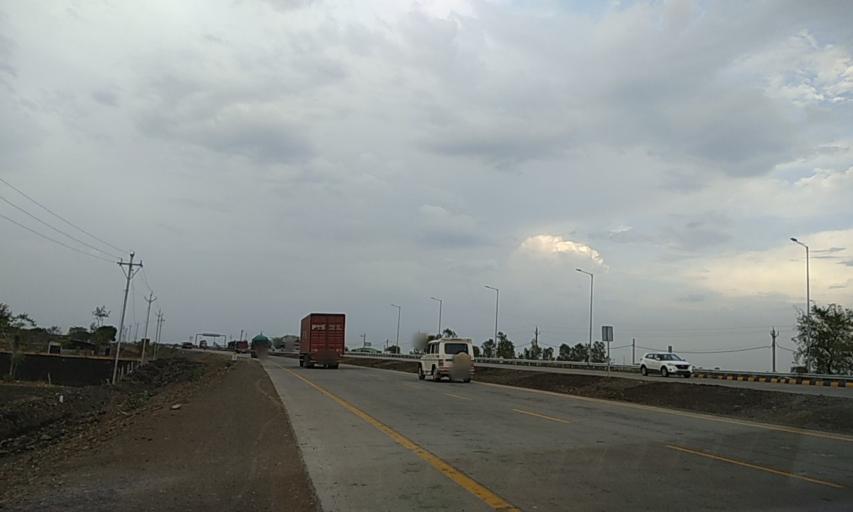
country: IN
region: Madhya Pradesh
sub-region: Shajapur
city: Shajapur
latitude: 23.4450
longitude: 76.3162
